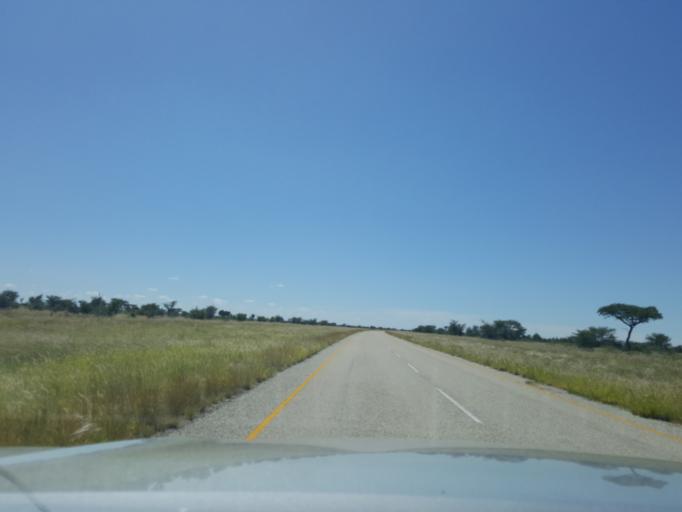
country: BW
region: Central
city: Gweta
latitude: -20.2226
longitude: 25.0184
